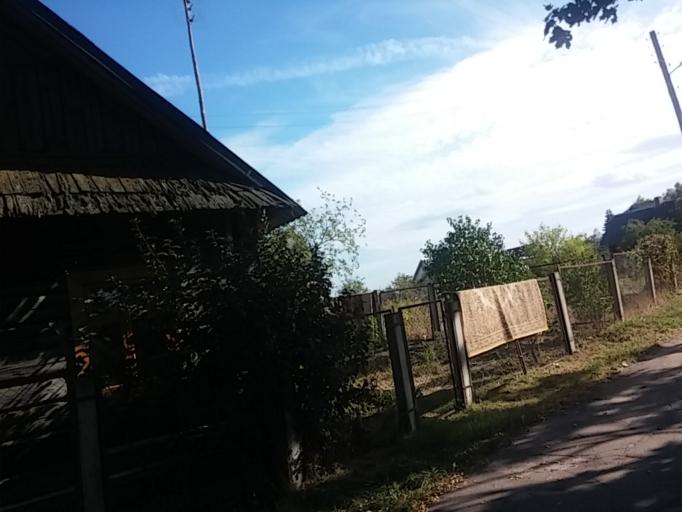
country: BY
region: Minsk
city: Chervyen'
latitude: 53.7756
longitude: 28.2661
